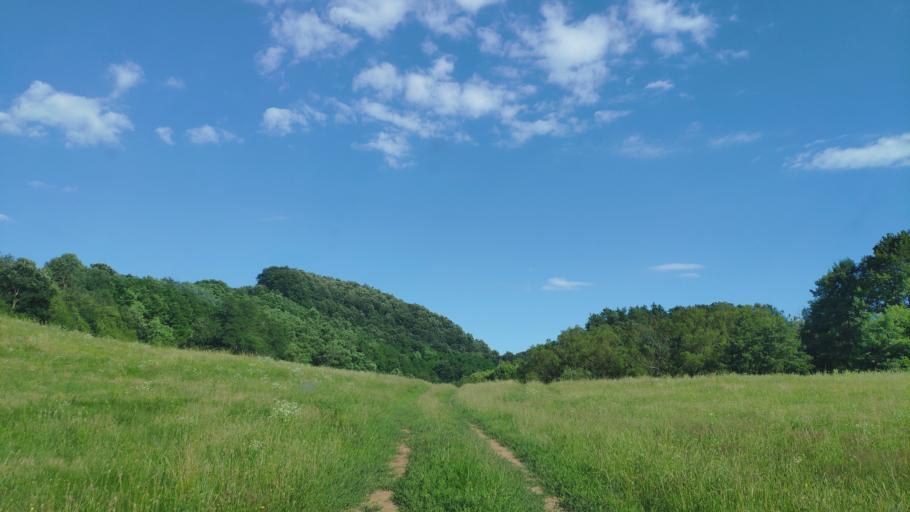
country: SK
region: Banskobystricky
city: Rimavska Sobota
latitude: 48.2462
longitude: 20.1026
